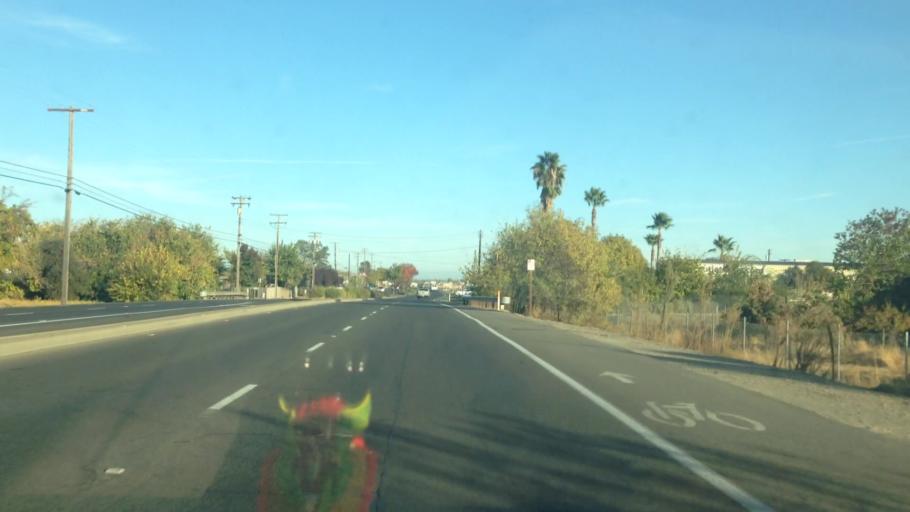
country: US
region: California
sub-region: Sacramento County
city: Rio Linda
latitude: 38.6905
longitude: -121.4104
